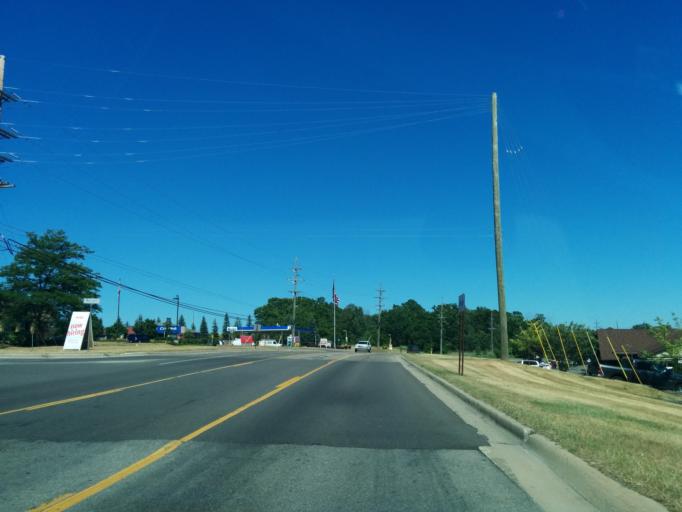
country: US
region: Michigan
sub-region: Oakland County
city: Wolverine Lake
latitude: 42.5431
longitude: -83.4436
